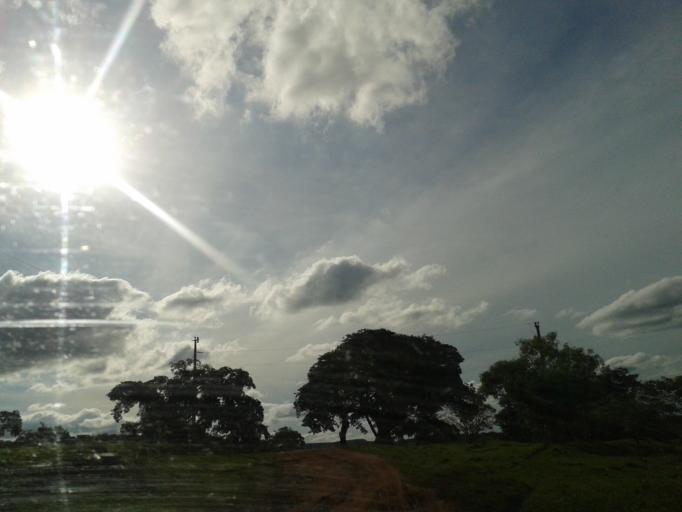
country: BR
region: Minas Gerais
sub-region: Campina Verde
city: Campina Verde
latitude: -19.4383
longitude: -49.7359
